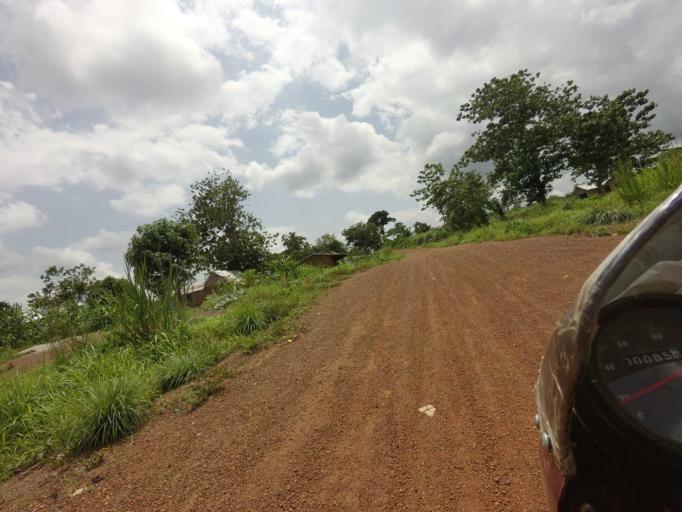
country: SL
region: Eastern Province
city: Daru
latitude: 7.9926
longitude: -10.8616
